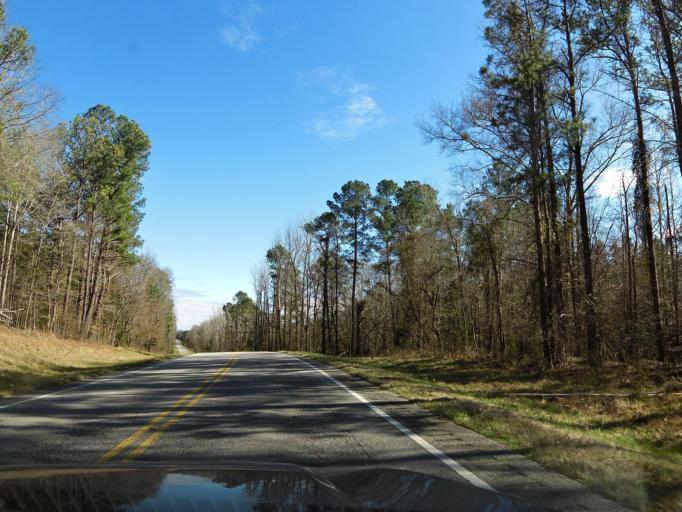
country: US
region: Alabama
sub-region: Barbour County
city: Clayton
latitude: 32.0369
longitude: -85.4073
